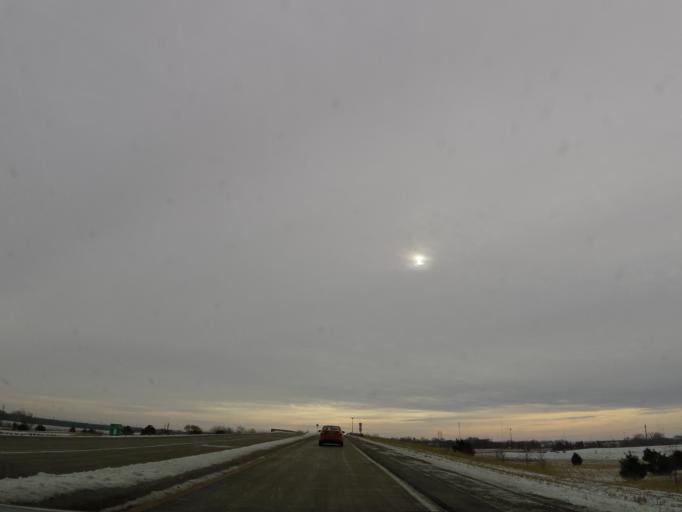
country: US
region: Illinois
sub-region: LaSalle County
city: Oglesby
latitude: 41.2774
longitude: -89.0834
